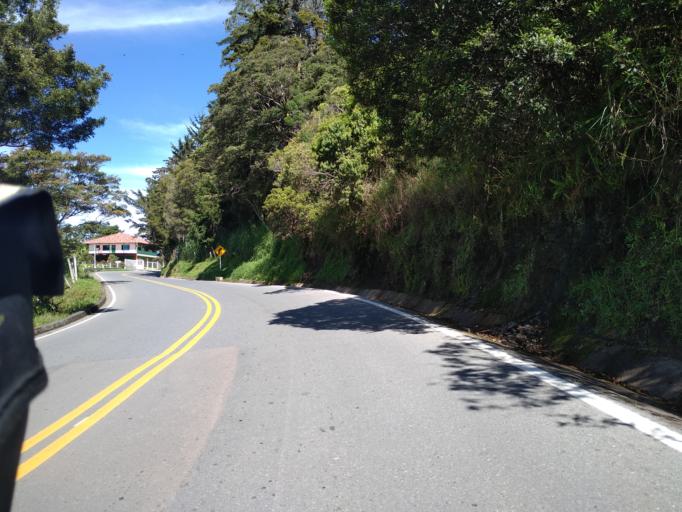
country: CO
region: Santander
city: Velez
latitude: 5.9986
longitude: -73.6863
